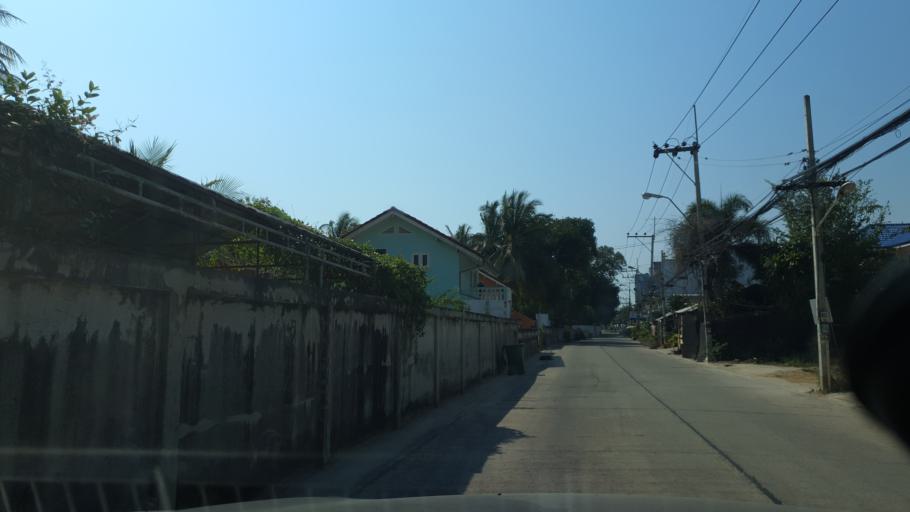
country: TH
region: Phetchaburi
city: Cha-am
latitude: 12.7863
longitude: 99.9788
